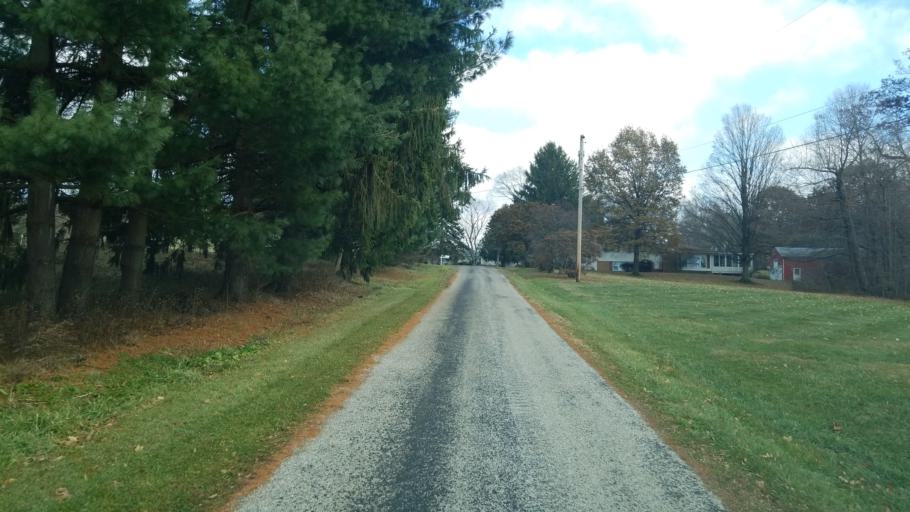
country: US
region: Ohio
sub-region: Ashland County
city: Ashland
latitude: 40.8265
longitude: -82.3808
